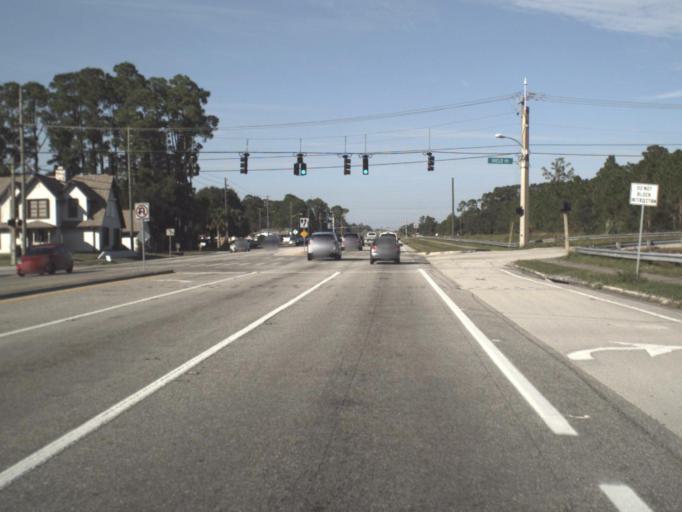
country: US
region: Florida
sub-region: Brevard County
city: June Park
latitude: 28.0387
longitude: -80.6713
